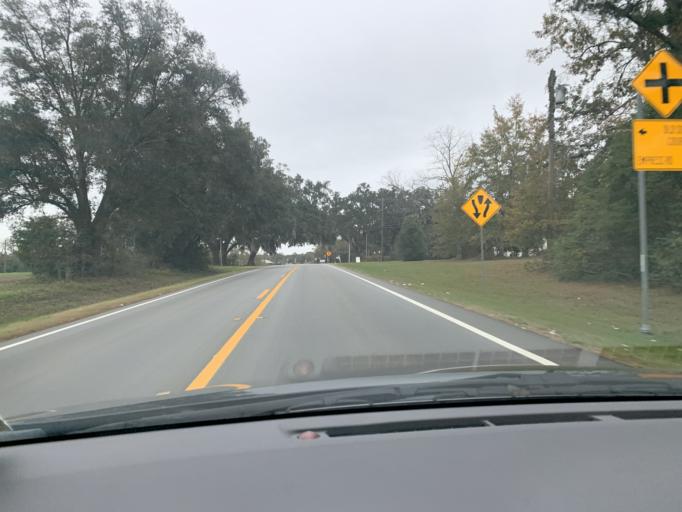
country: US
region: Georgia
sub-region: Brooks County
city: Quitman
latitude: 30.7698
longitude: -83.5643
